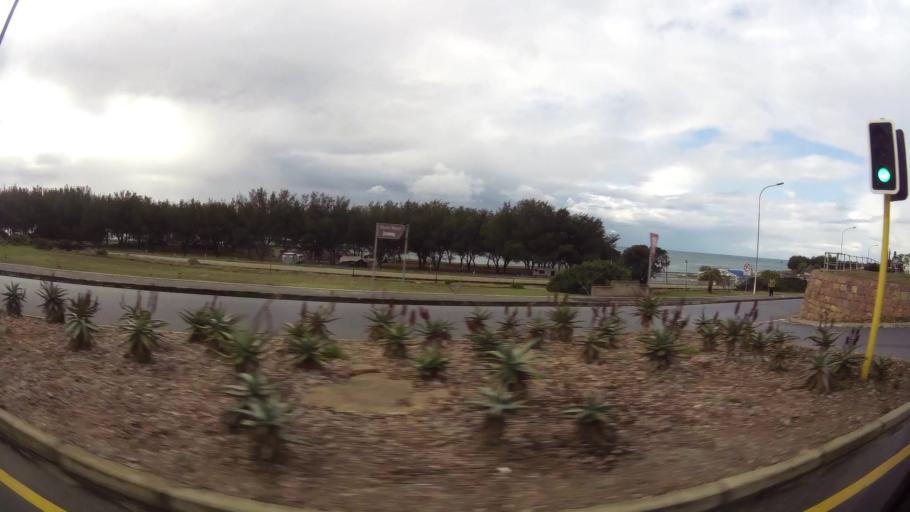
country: ZA
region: Western Cape
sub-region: Eden District Municipality
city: Mossel Bay
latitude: -34.1727
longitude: 22.1253
